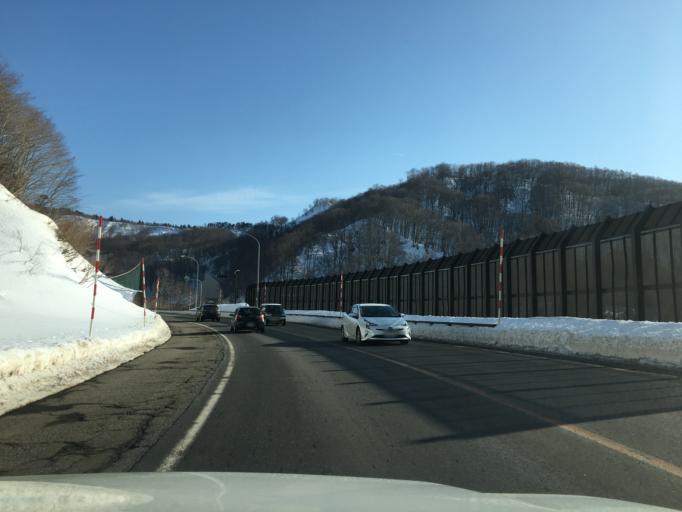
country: JP
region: Yamagata
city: Tsuruoka
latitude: 38.5578
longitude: 139.9289
